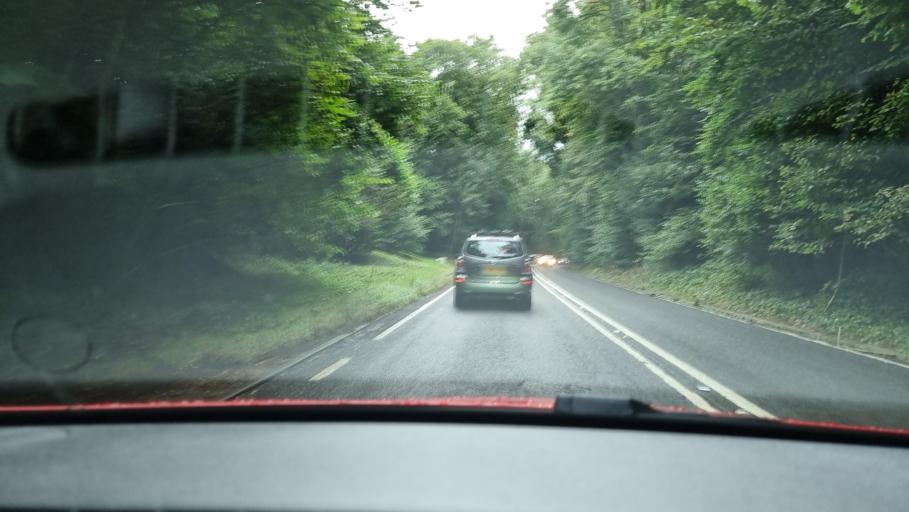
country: GB
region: England
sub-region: Hertfordshire
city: Berkhamsted
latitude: 51.7461
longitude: -0.5816
